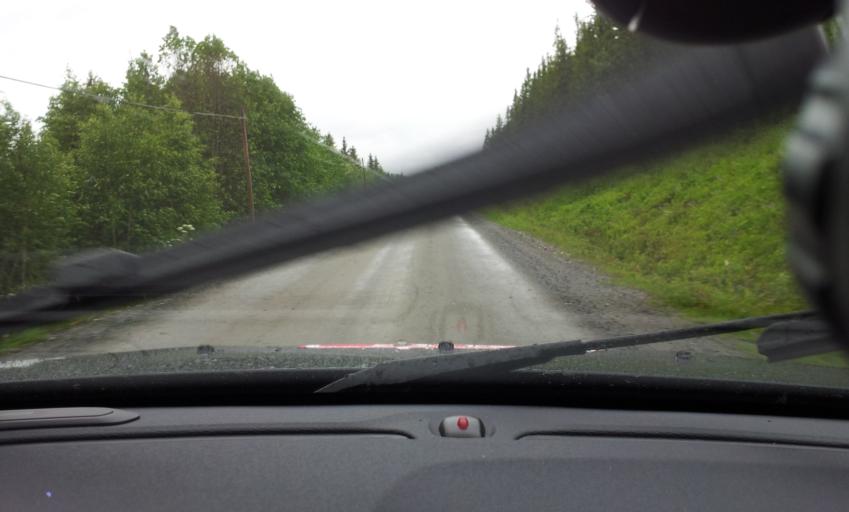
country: SE
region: Jaemtland
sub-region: Are Kommun
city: Are
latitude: 63.4885
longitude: 12.7720
